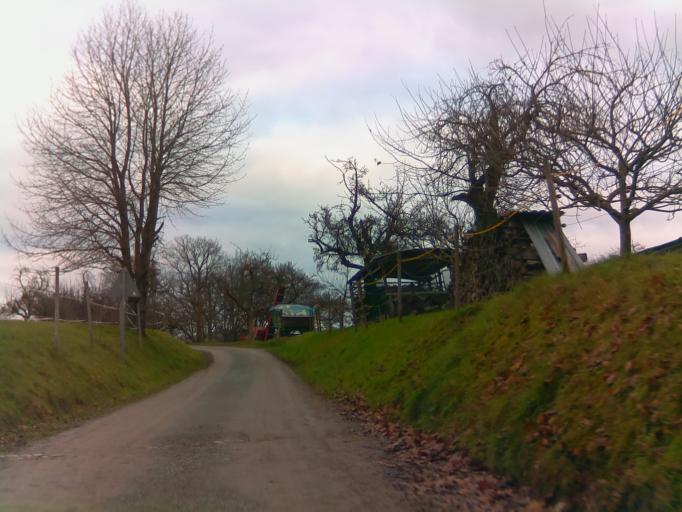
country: DE
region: Bavaria
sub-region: Regierungsbezirk Unterfranken
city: Hausen
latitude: 49.8721
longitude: 9.2077
